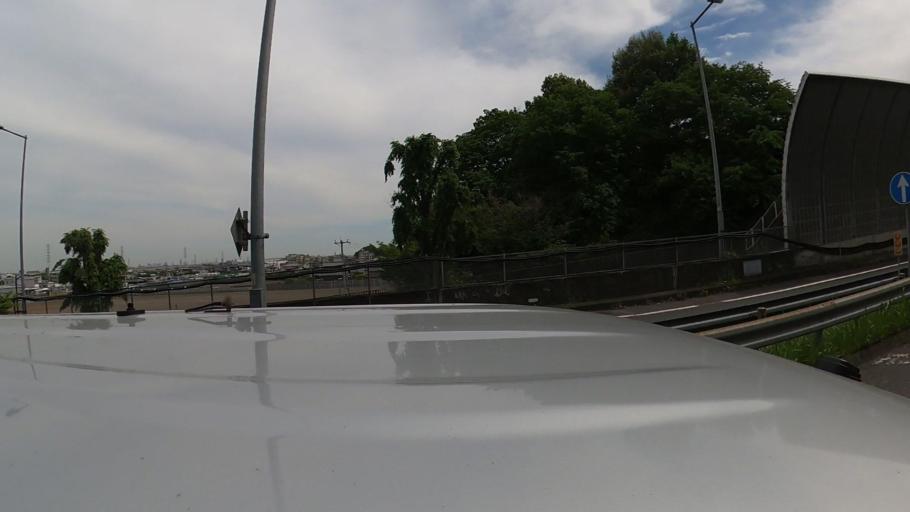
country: JP
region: Saitama
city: Wako
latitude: 35.7998
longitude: 139.6188
